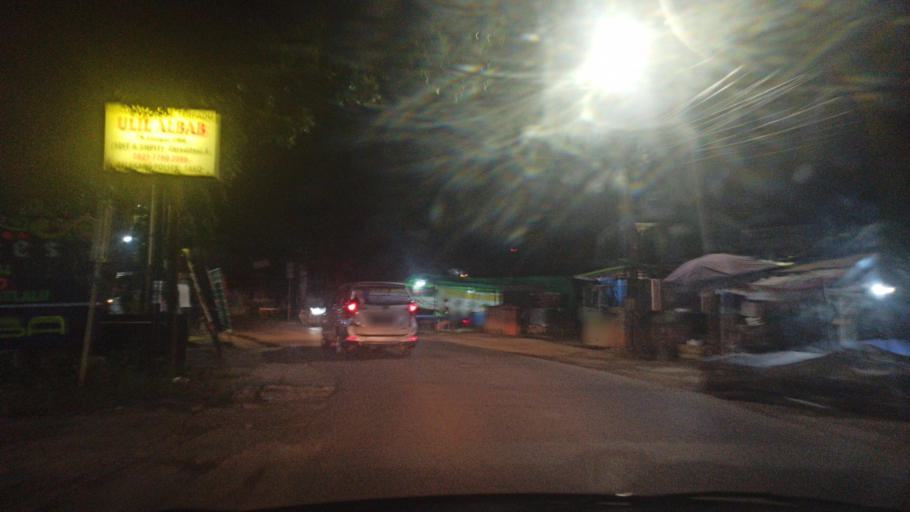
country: ID
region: South Sumatra
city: Palembang
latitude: -2.9222
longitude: 104.7842
